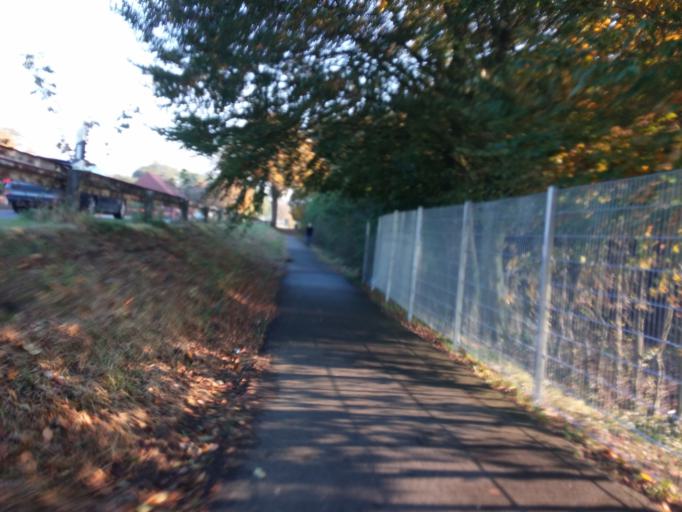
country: DE
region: North Rhine-Westphalia
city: Dorsten
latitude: 51.6285
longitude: 7.0067
